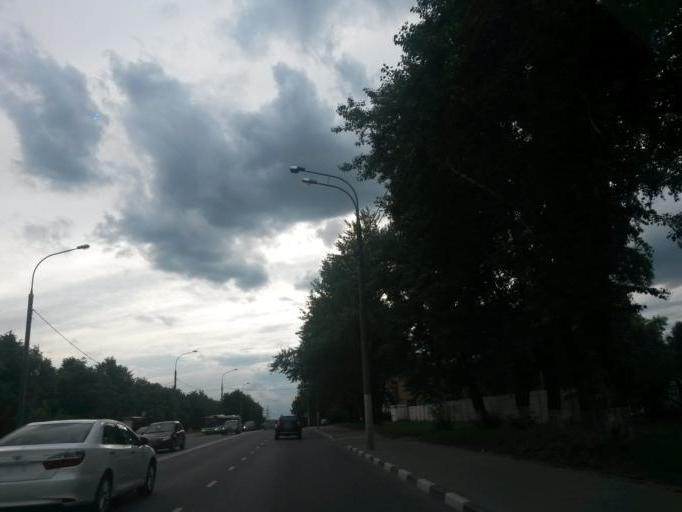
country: RU
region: Moscow
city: Mar'ino
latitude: 55.6357
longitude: 37.7116
